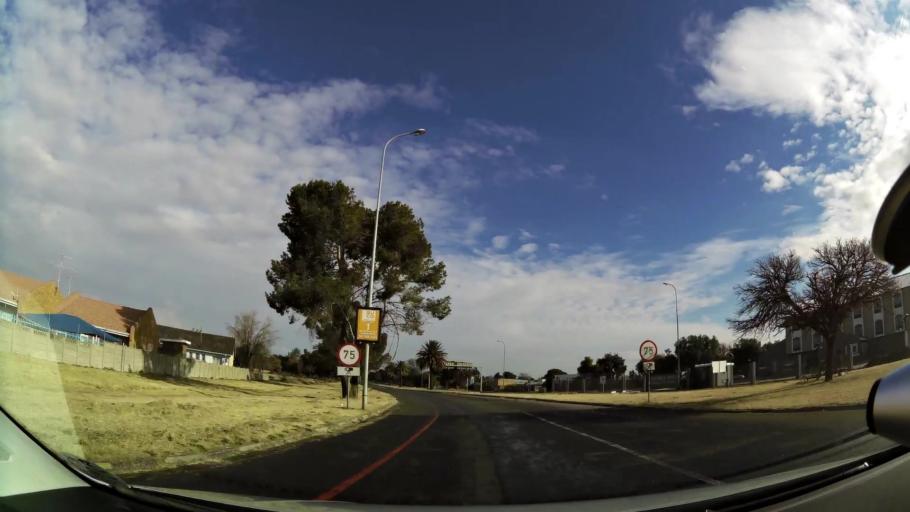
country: ZA
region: Orange Free State
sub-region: Lejweleputswa District Municipality
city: Welkom
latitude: -27.9678
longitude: 26.7651
